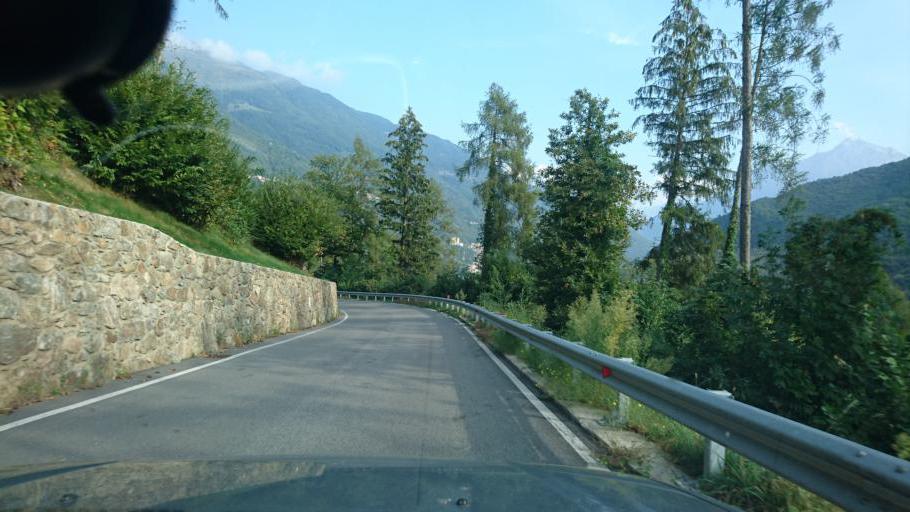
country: IT
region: Lombardy
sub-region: Provincia di Brescia
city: Berzo
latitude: 46.0961
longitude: 10.3100
